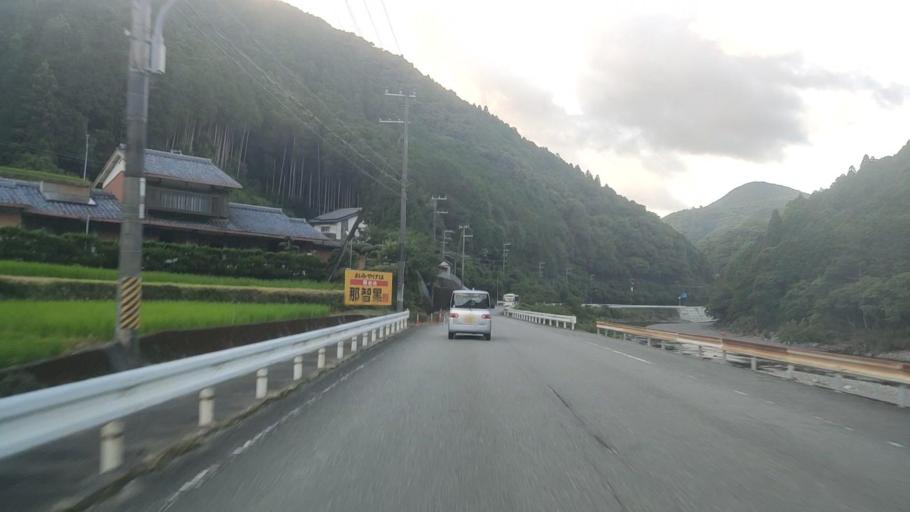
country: JP
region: Wakayama
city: Tanabe
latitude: 33.7840
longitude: 135.5053
